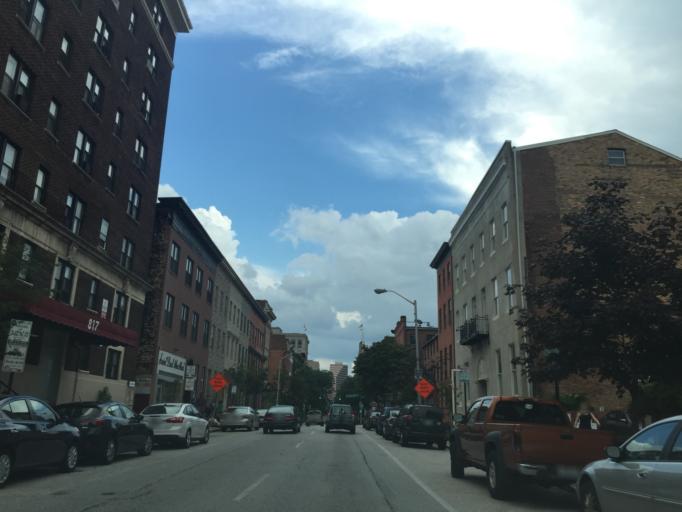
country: US
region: Maryland
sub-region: City of Baltimore
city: Baltimore
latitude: 39.2997
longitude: -76.6142
